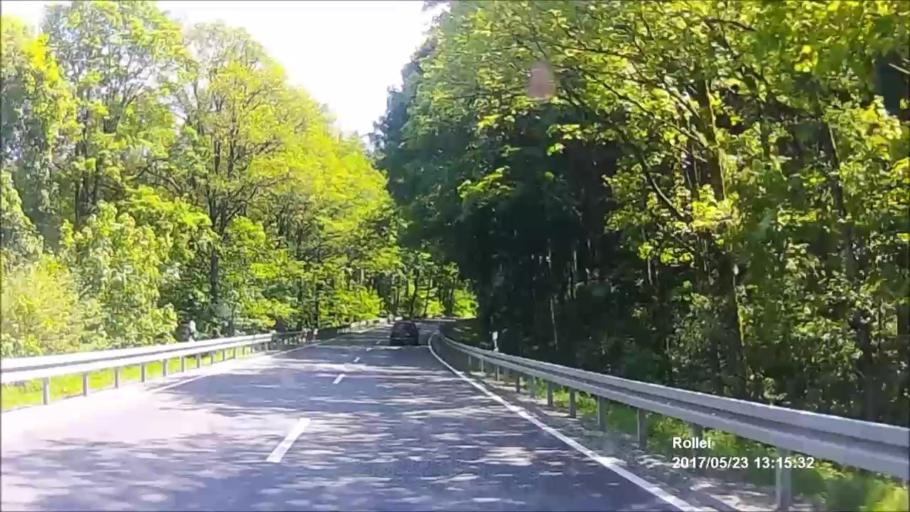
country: DE
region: Bavaria
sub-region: Upper Bavaria
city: Hohenpolding
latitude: 48.4022
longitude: 12.1288
